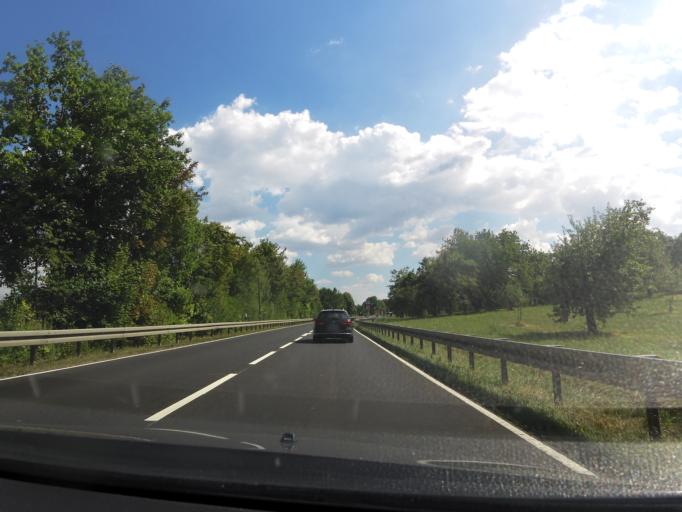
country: DE
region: Bavaria
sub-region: Regierungsbezirk Unterfranken
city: Margetshochheim
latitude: 49.8451
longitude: 9.8587
